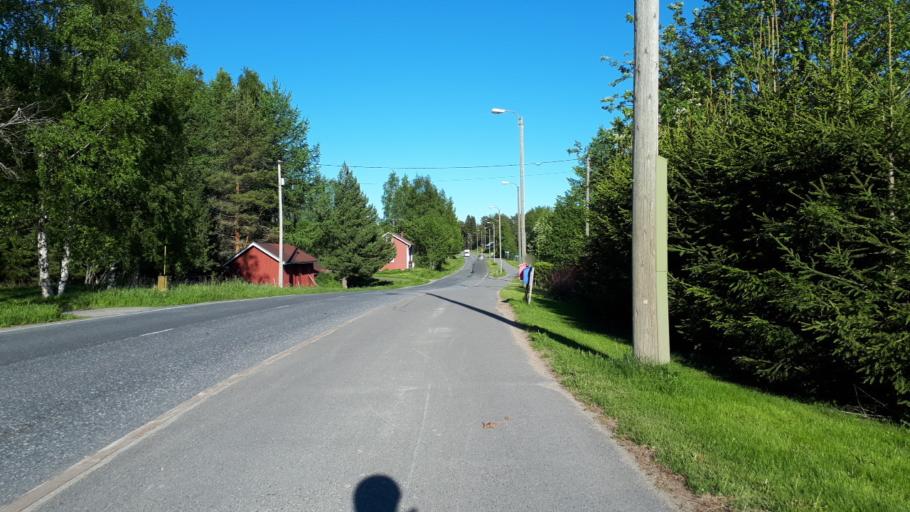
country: FI
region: Northern Ostrobothnia
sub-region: Oulunkaari
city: Ii
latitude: 65.3230
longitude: 25.4515
